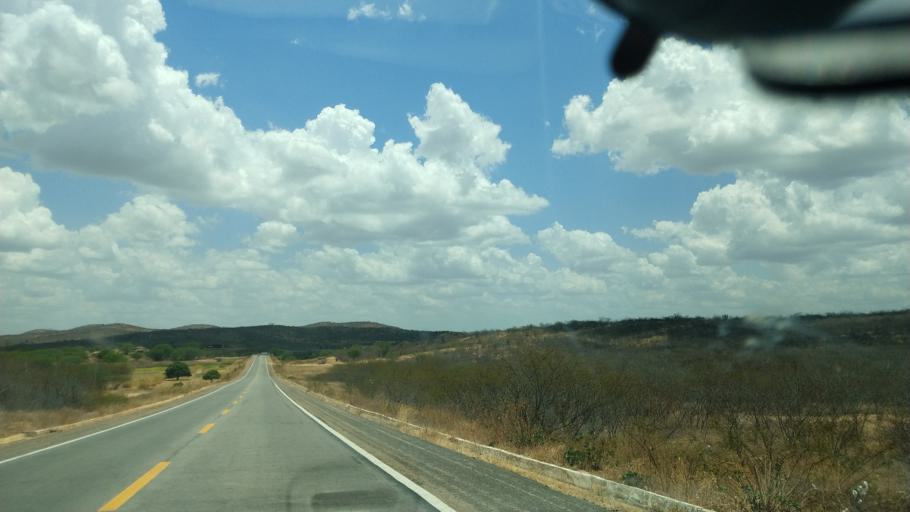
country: BR
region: Rio Grande do Norte
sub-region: Currais Novos
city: Currais Novos
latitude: -6.2513
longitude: -36.4751
